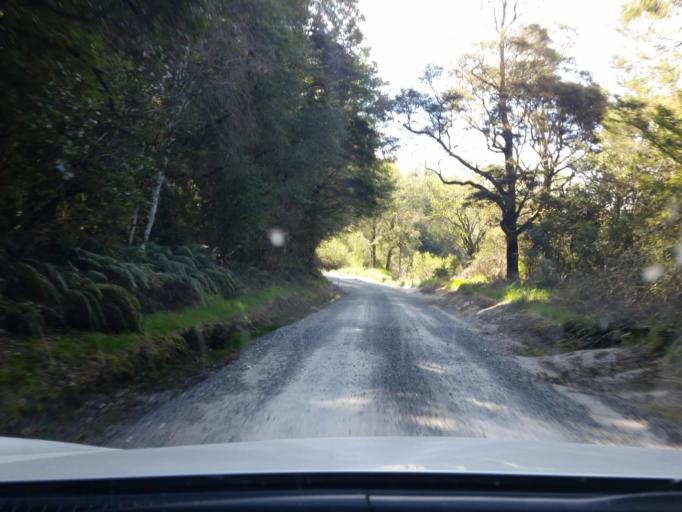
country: NZ
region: West Coast
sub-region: Buller District
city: Westport
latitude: -41.8754
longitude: 172.2472
